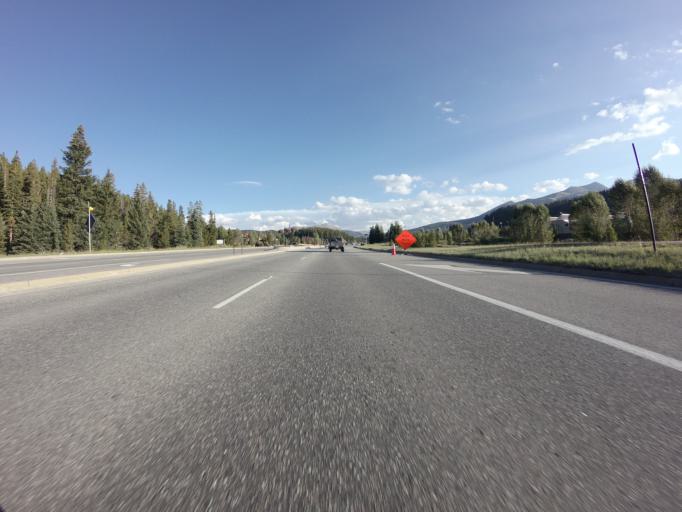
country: US
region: Colorado
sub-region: Summit County
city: Breckenridge
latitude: 39.4971
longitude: -106.0461
